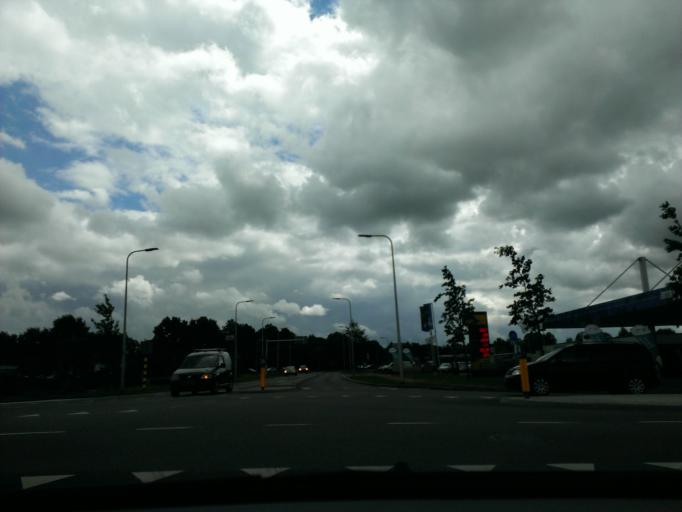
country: NL
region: Drenthe
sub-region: Gemeente Hoogeveen
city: Hoogeveen
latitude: 52.7312
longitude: 6.5039
